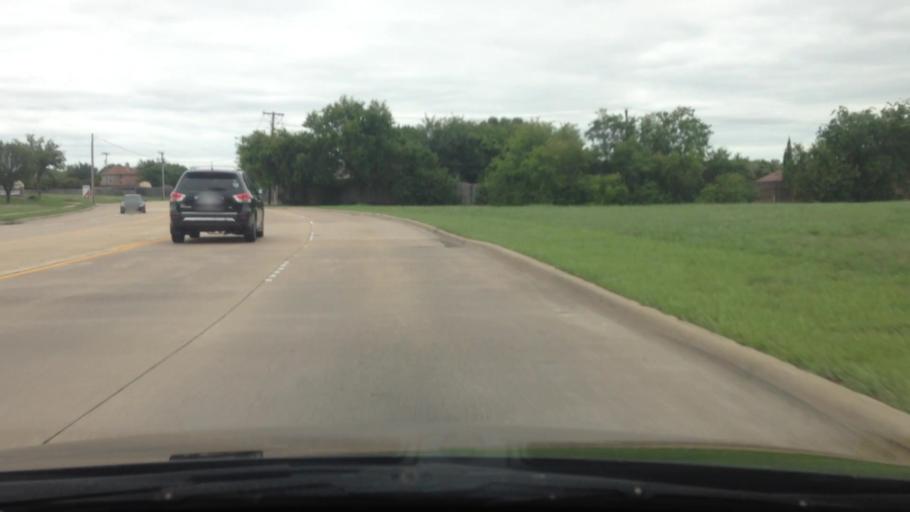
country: US
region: Texas
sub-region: Tarrant County
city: Watauga
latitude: 32.8907
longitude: -97.2386
